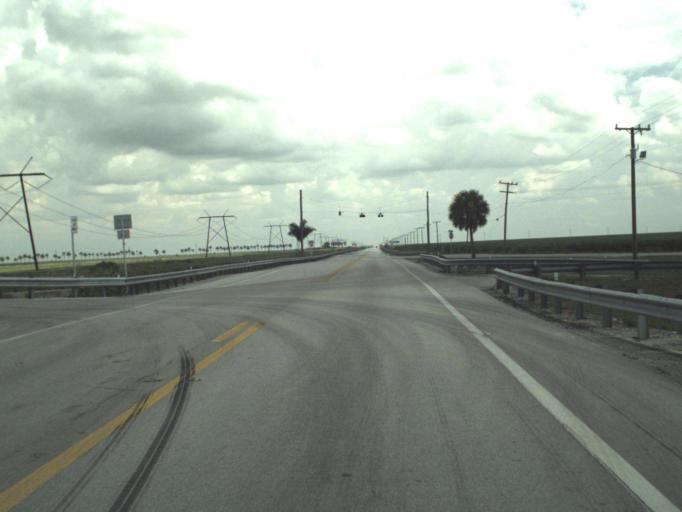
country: US
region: Florida
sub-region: Palm Beach County
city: Pahokee
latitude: 26.8133
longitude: -80.5642
